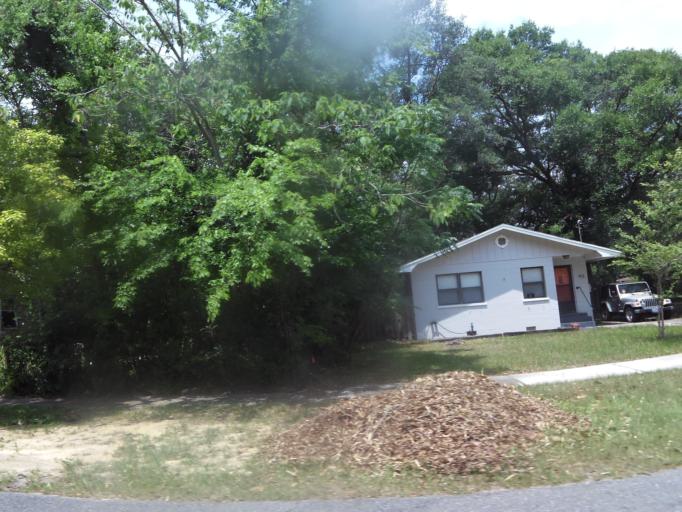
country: US
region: Florida
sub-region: Nassau County
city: Fernandina Beach
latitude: 30.6648
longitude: -81.4581
